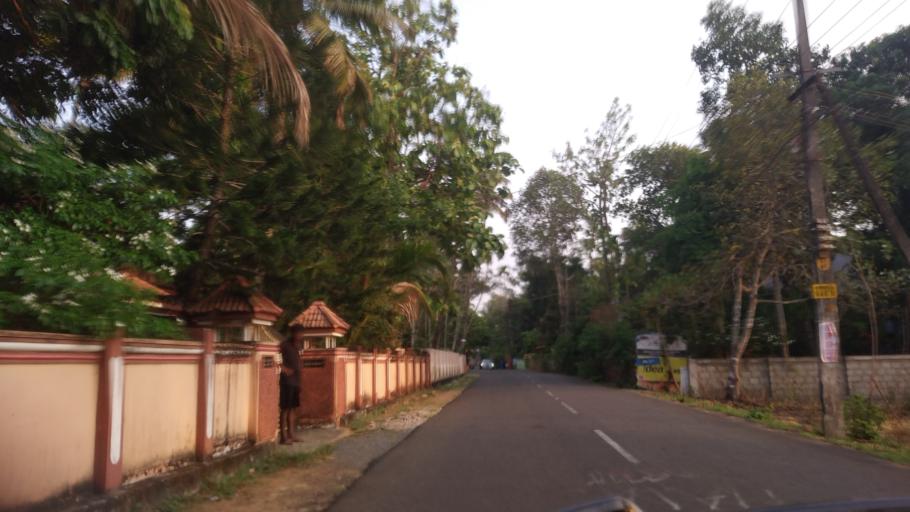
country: IN
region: Kerala
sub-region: Thrissur District
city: Thanniyam
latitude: 10.3318
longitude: 76.1209
